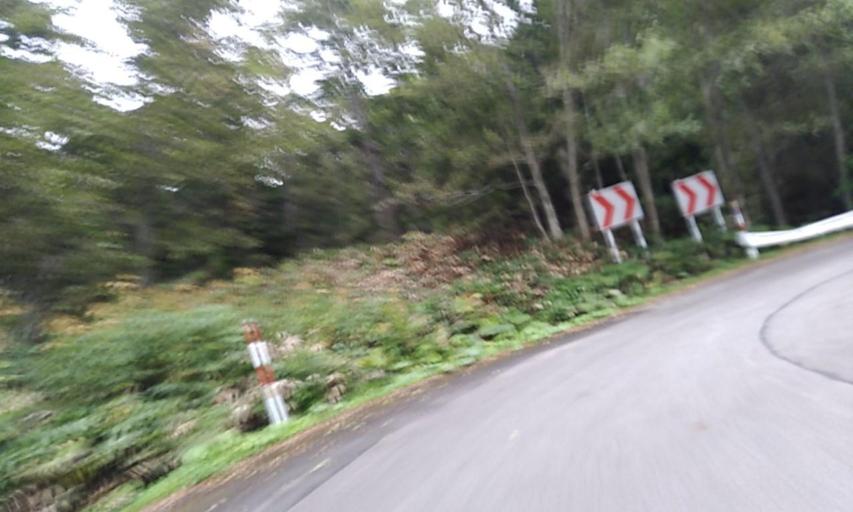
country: JP
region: Hokkaido
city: Bihoro
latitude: 43.5665
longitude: 144.1953
